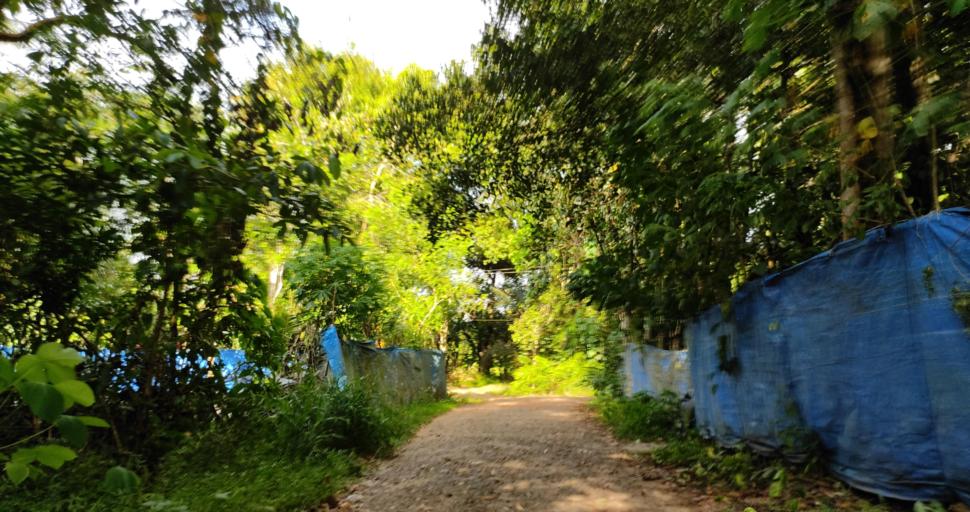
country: IN
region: Kerala
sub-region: Alappuzha
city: Shertallai
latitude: 9.6225
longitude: 76.3340
